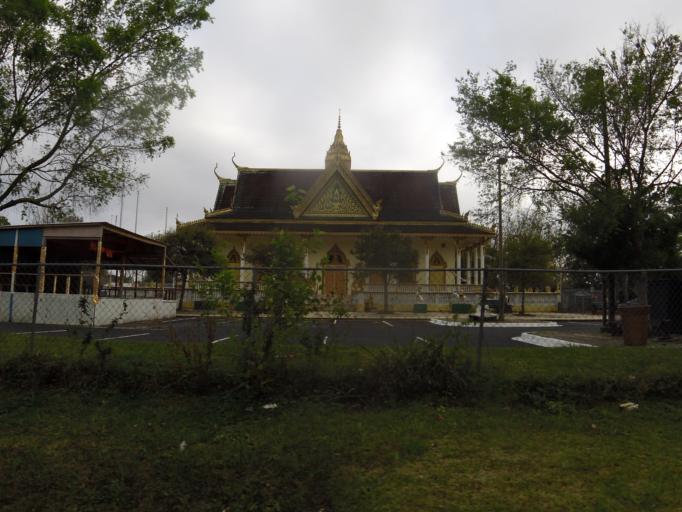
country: US
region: Florida
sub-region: Duval County
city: Jacksonville
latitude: 30.3240
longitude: -81.7181
